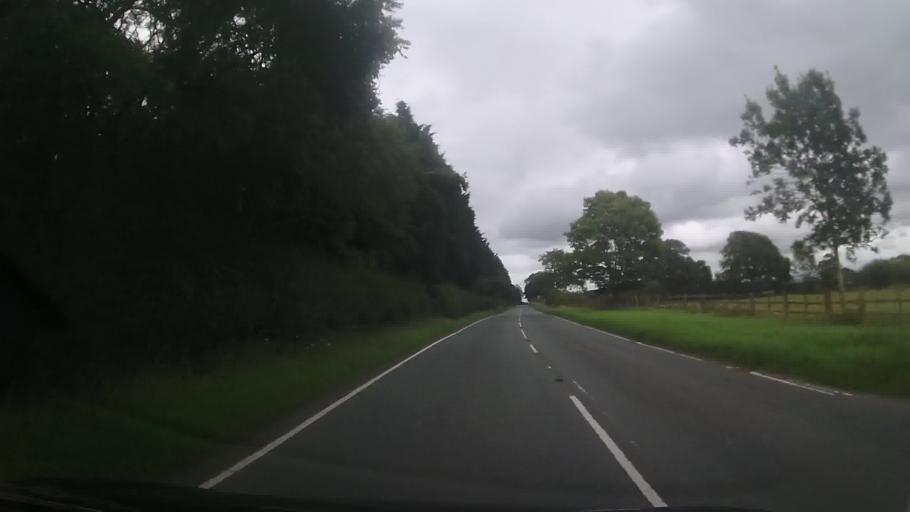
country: GB
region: England
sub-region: Shropshire
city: Ellesmere
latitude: 52.9275
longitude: -2.8108
